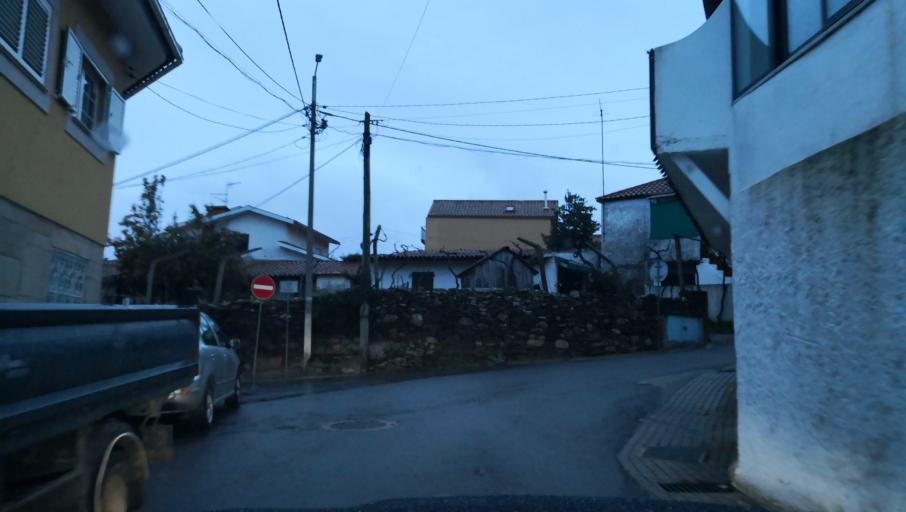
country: PT
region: Vila Real
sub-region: Vila Real
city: Vila Real
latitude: 41.2806
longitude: -7.7404
